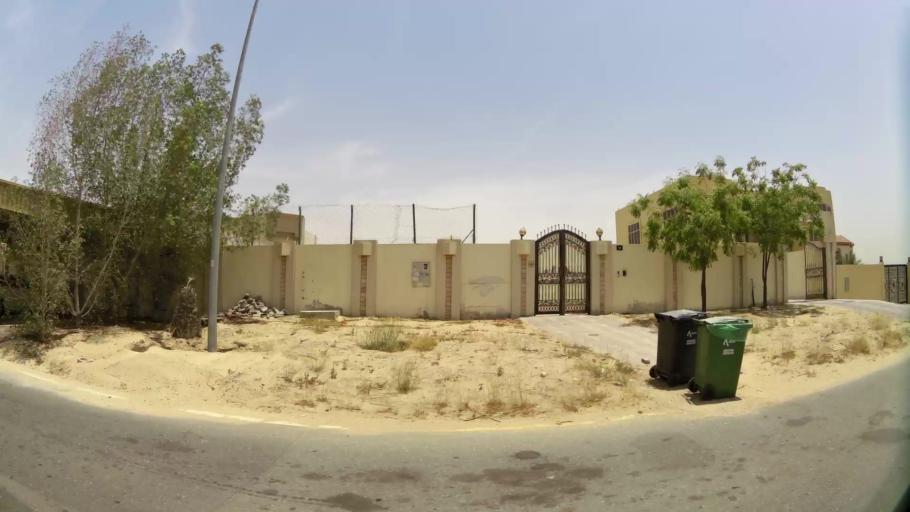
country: AE
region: Ash Shariqah
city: Sharjah
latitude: 25.2517
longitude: 55.4673
